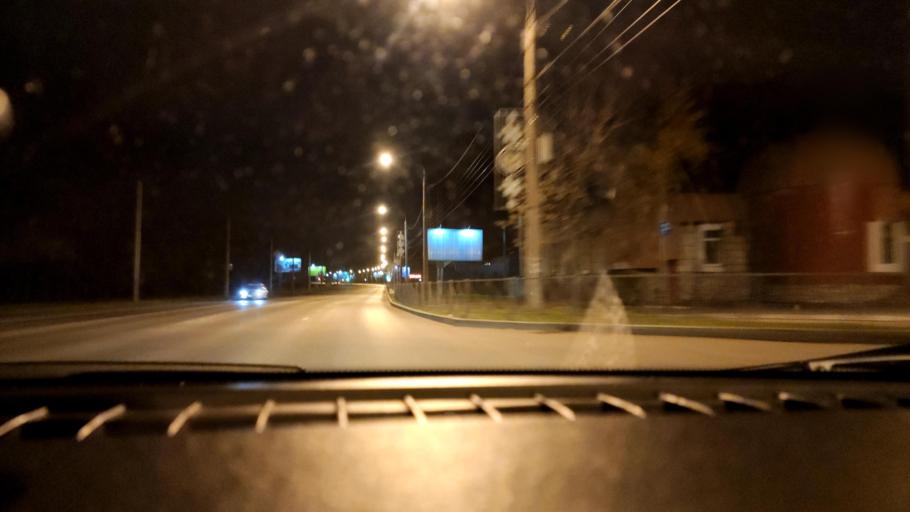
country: RU
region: Perm
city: Kondratovo
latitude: 57.9787
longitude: 56.1687
